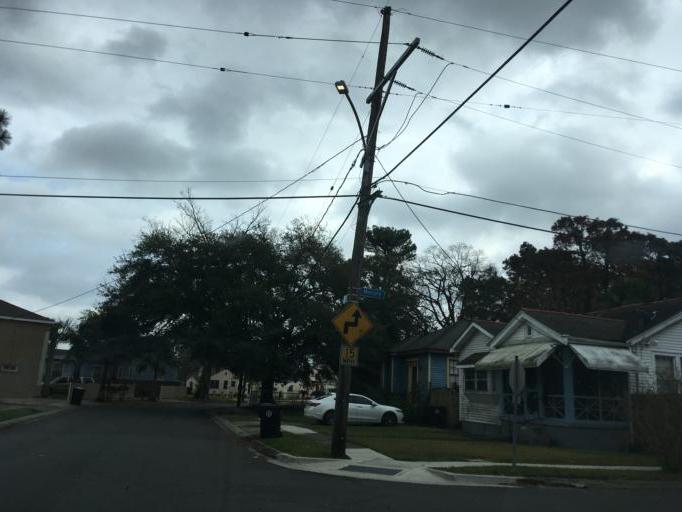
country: US
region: Louisiana
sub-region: Orleans Parish
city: New Orleans
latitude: 29.9960
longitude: -90.0578
